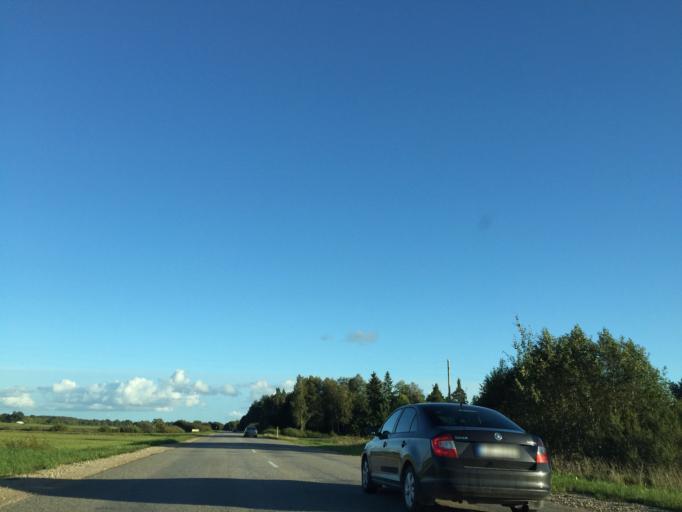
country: LV
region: Kuldigas Rajons
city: Kuldiga
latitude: 56.9547
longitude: 22.0083
